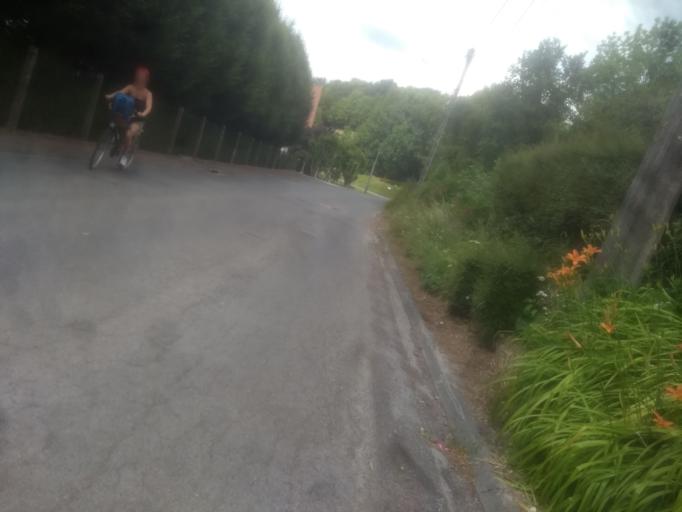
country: FR
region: Nord-Pas-de-Calais
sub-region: Departement du Pas-de-Calais
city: Mont-Saint-Eloi
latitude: 50.3392
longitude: 2.6914
